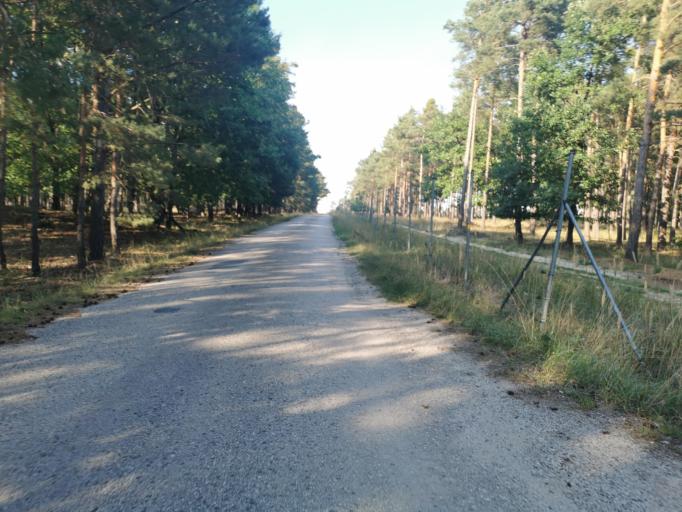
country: SK
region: Trnavsky
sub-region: Okres Senica
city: Senica
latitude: 48.6366
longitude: 17.2986
